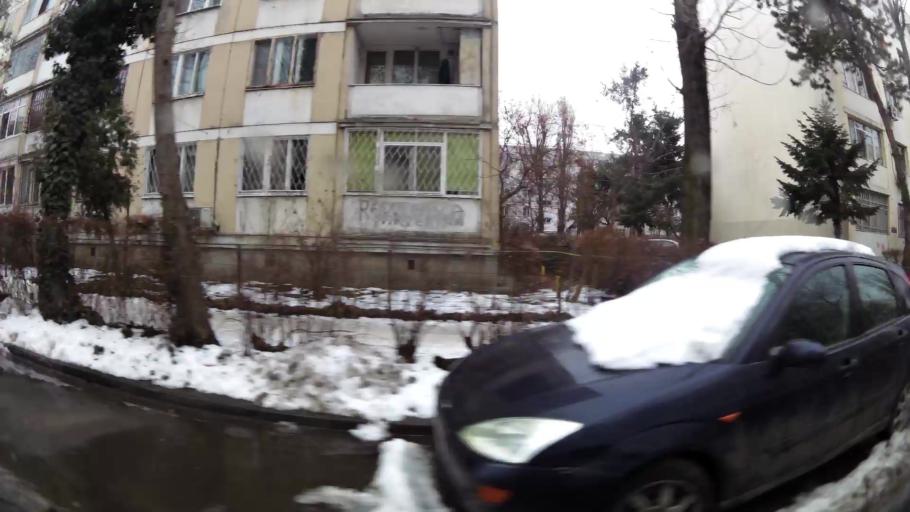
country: RO
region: Ilfov
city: Dobroesti
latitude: 44.4221
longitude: 26.1679
